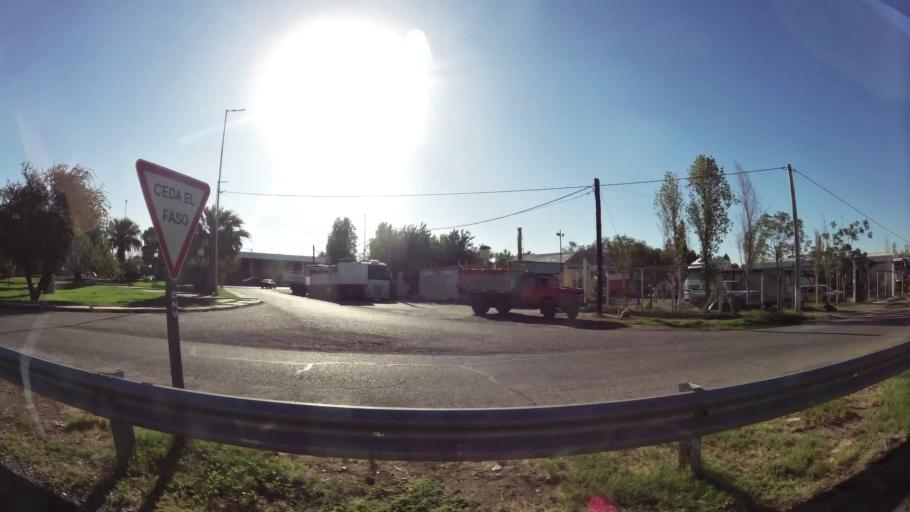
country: AR
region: San Juan
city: Villa Krause
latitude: -31.5720
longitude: -68.5182
